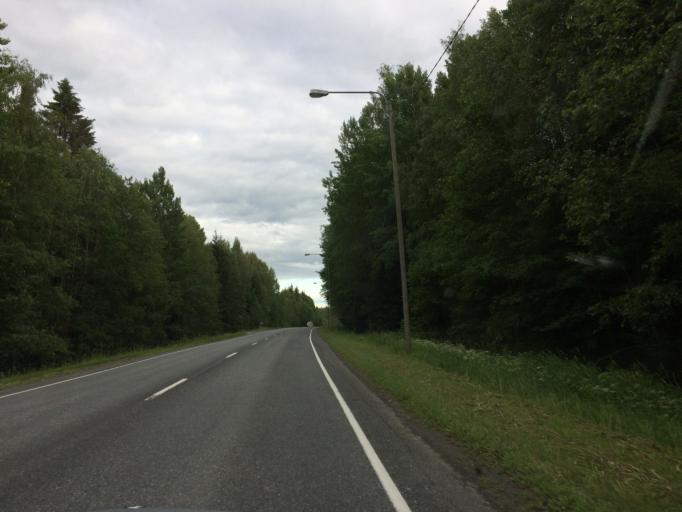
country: FI
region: Haeme
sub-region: Haemeenlinna
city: Haemeenlinna
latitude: 60.9460
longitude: 24.5139
